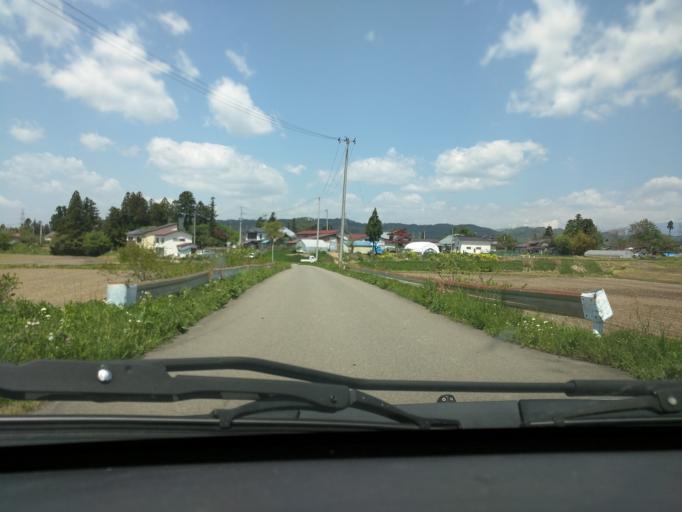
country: JP
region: Fukushima
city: Kitakata
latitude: 37.6077
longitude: 139.8481
